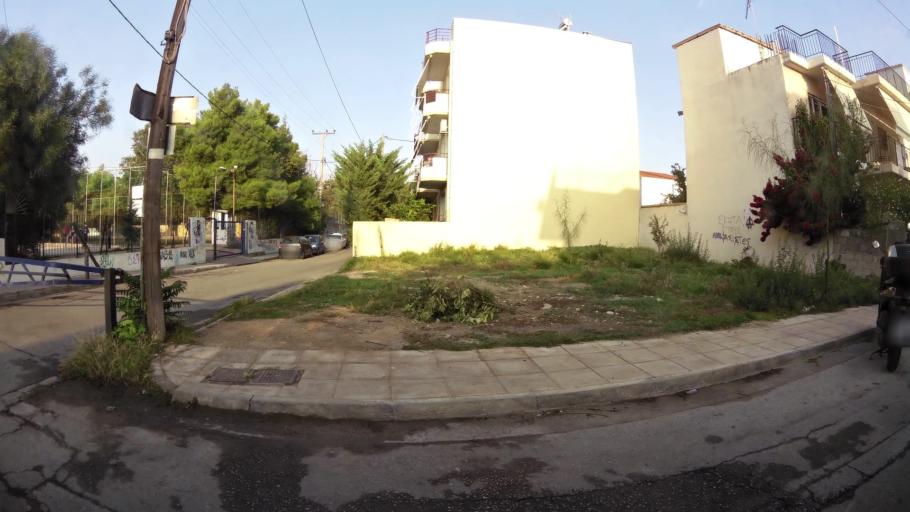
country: GR
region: Attica
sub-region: Nomarchia Dytikis Attikis
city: Zefyri
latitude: 38.0502
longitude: 23.7229
